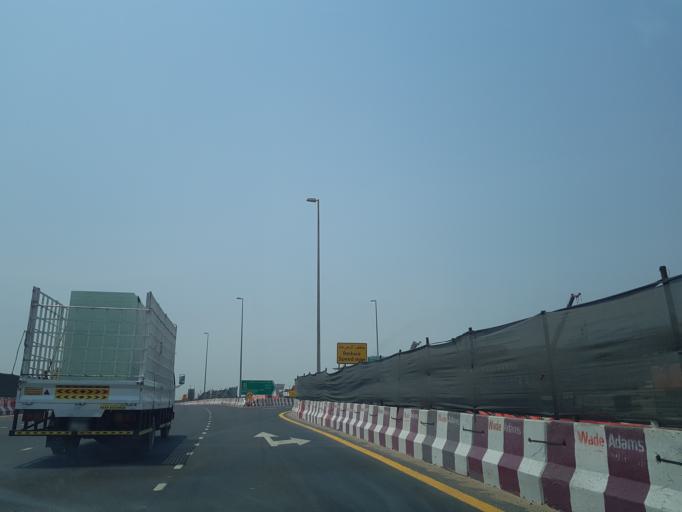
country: AE
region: Dubai
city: Dubai
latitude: 24.9968
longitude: 55.1894
